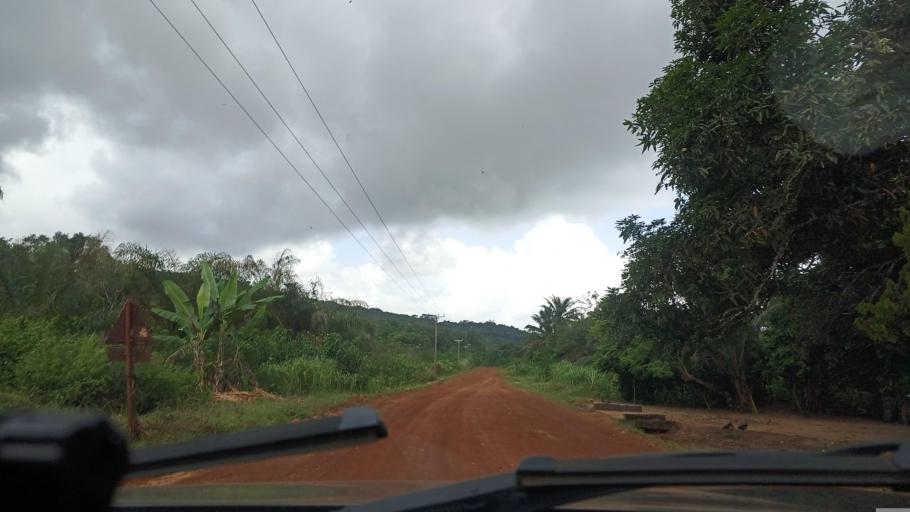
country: LR
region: Grand Cape Mount
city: Robertsport
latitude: 6.7076
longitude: -11.3341
